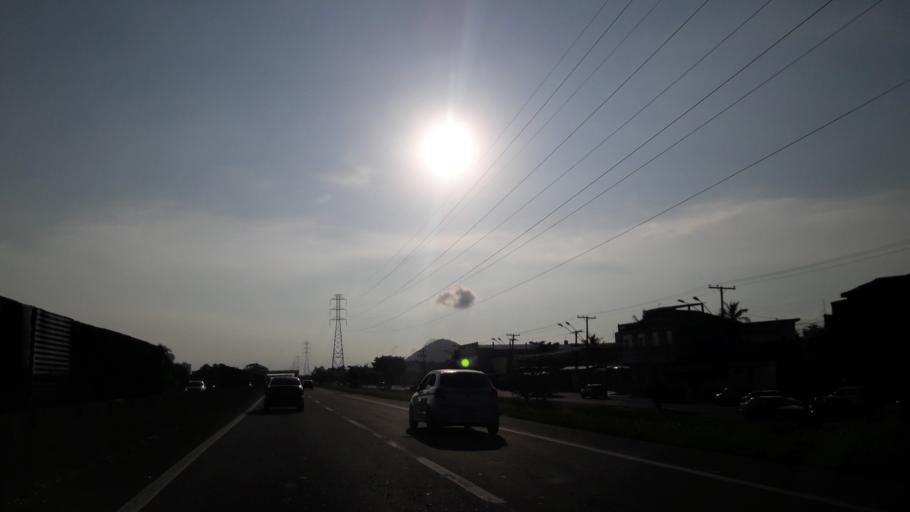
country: BR
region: Sao Paulo
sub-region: Mongagua
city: Mongagua
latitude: -24.1065
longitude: -46.6472
